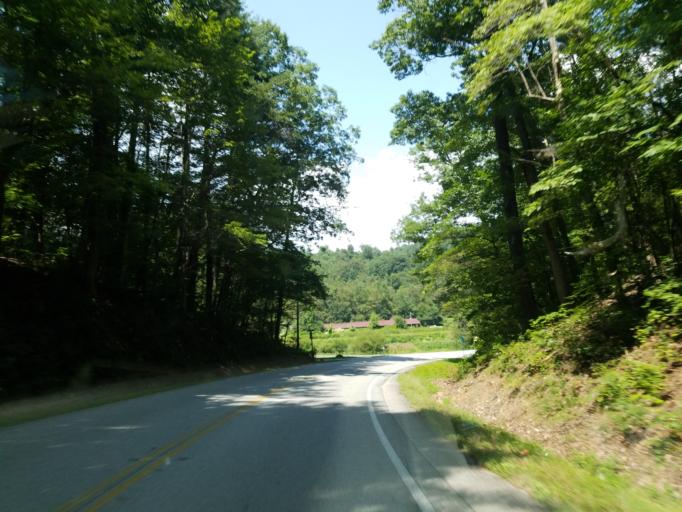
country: US
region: Georgia
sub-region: Lumpkin County
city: Dahlonega
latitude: 34.6564
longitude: -83.9084
